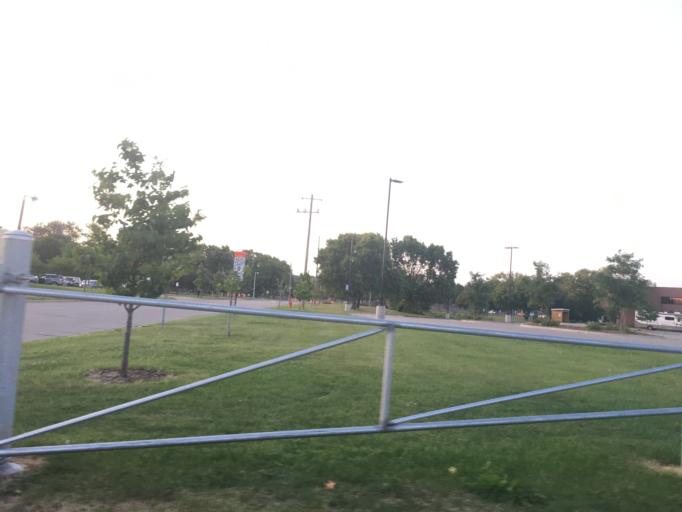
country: US
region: Minnesota
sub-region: Olmsted County
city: Rochester
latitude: 44.0200
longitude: -92.4386
